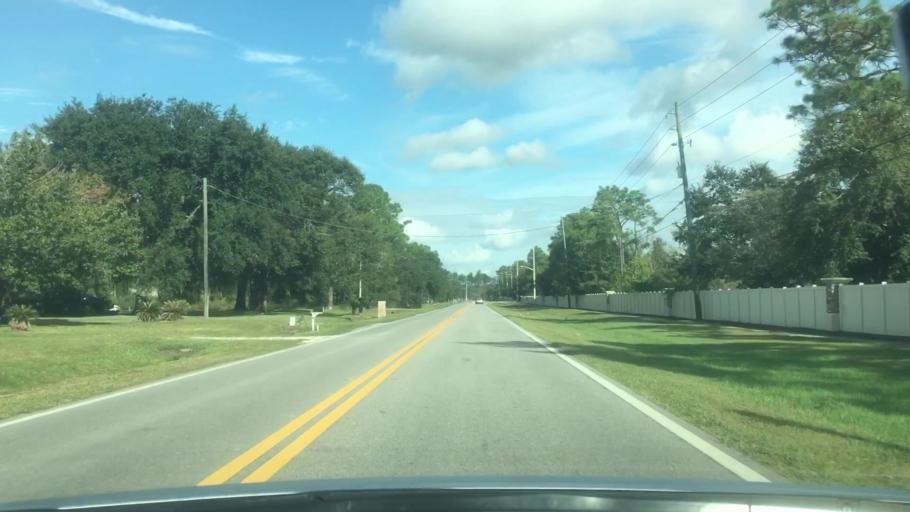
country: US
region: Florida
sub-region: Nassau County
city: Yulee
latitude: 30.4939
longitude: -81.5755
